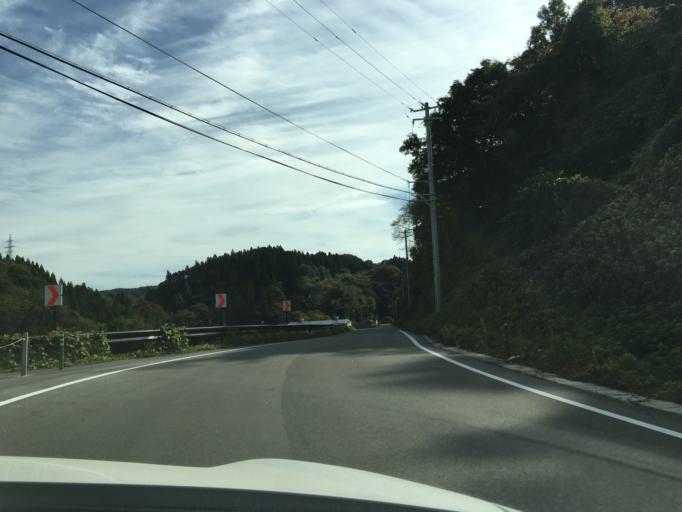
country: JP
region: Fukushima
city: Miharu
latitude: 37.5226
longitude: 140.5048
